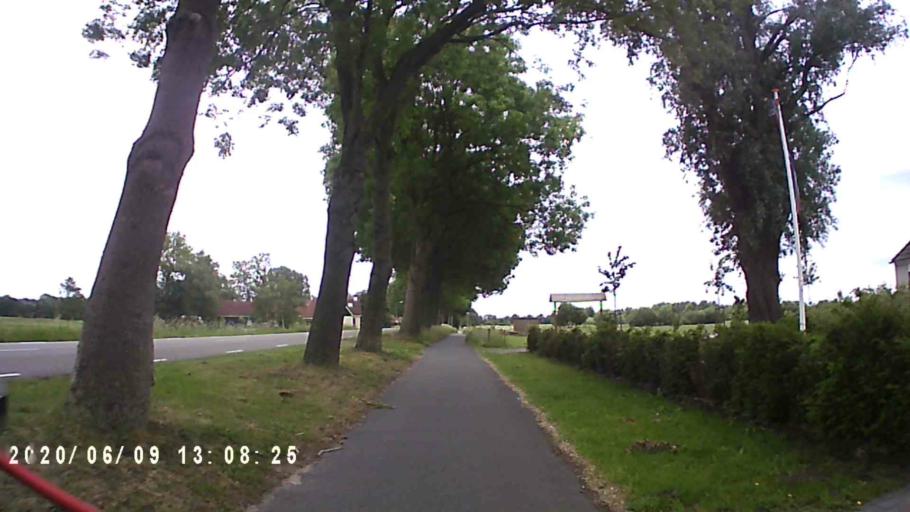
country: NL
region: Groningen
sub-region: Gemeente Haren
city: Haren
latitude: 53.2152
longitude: 6.6511
